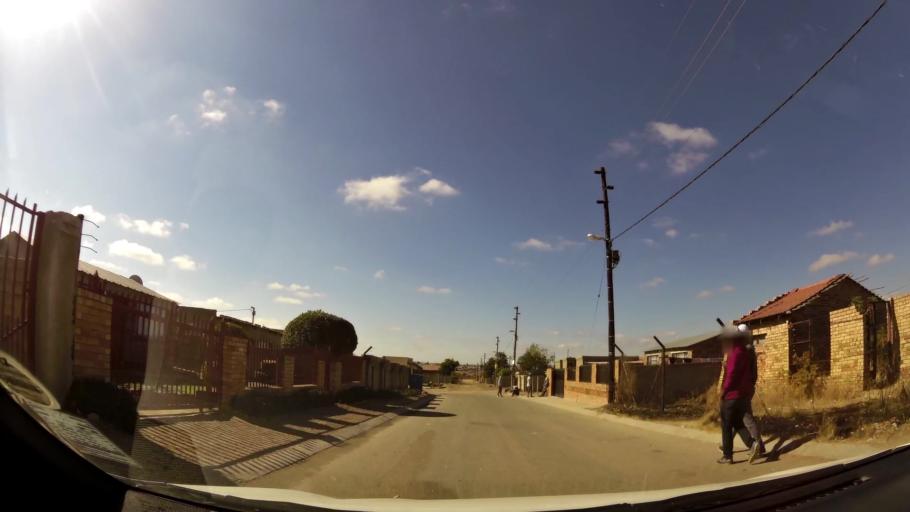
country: ZA
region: Limpopo
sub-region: Capricorn District Municipality
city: Polokwane
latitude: -23.8696
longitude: 29.3890
